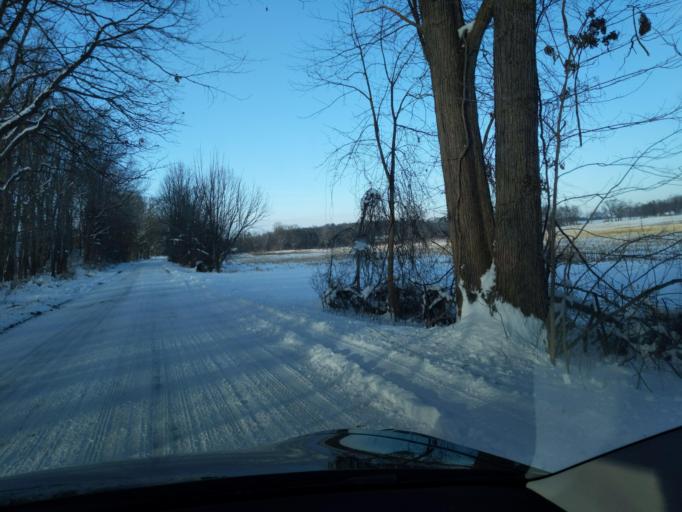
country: US
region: Michigan
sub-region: Ingham County
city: Stockbridge
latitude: 42.4636
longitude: -84.1057
